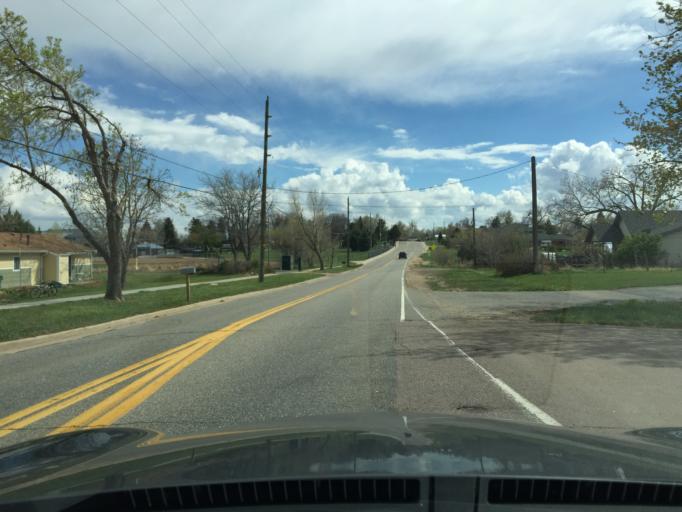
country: US
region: Colorado
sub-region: Boulder County
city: Lafayette
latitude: 40.0040
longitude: -105.0933
